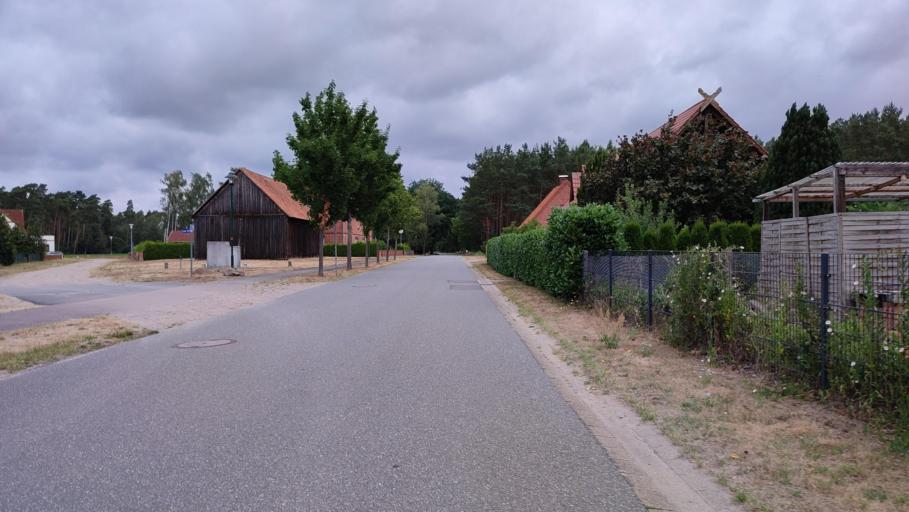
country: DE
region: Lower Saxony
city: Hitzacker
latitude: 53.1857
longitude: 11.1053
